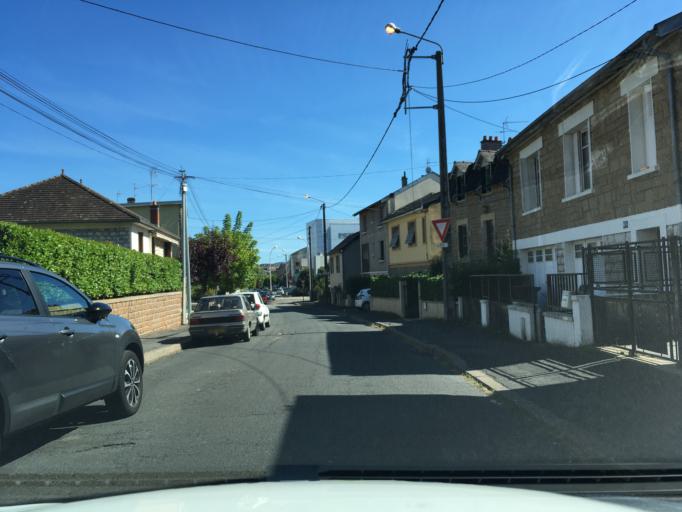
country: FR
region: Limousin
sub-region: Departement de la Correze
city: Brive-la-Gaillarde
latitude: 45.1681
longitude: 1.5270
